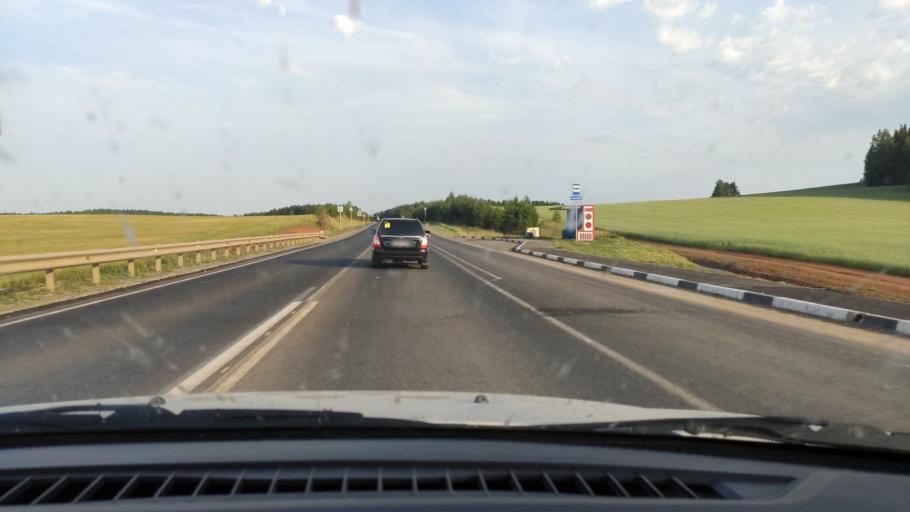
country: RU
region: Perm
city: Siva
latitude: 58.4134
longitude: 54.4674
